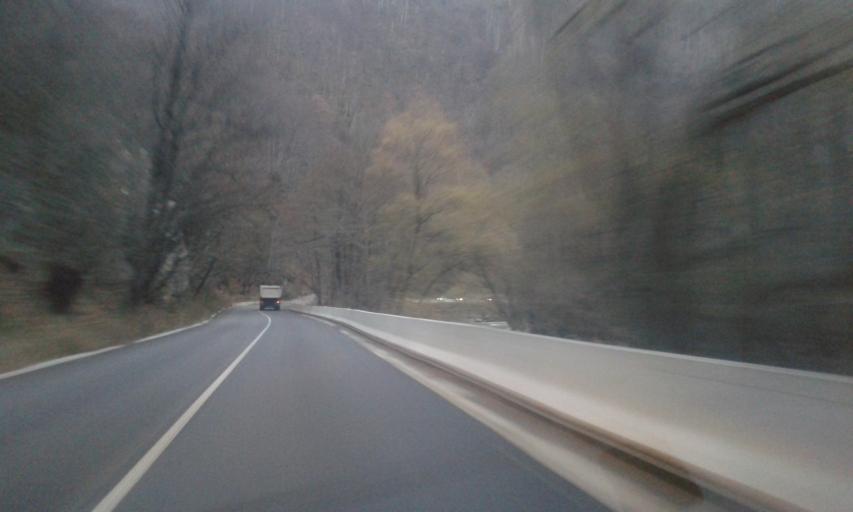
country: RO
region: Gorj
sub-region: Comuna Bumbesti-Jiu
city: Bumbesti-Jiu
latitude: 45.2402
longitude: 23.3934
